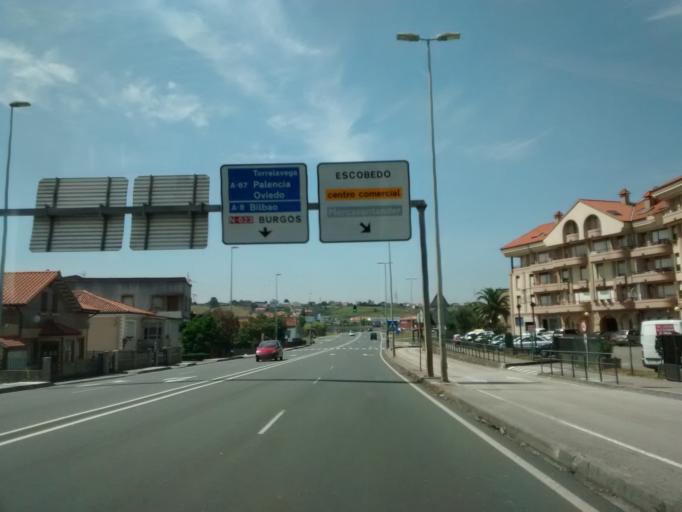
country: ES
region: Cantabria
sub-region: Provincia de Cantabria
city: Camargo
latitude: 43.4418
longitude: -3.8587
